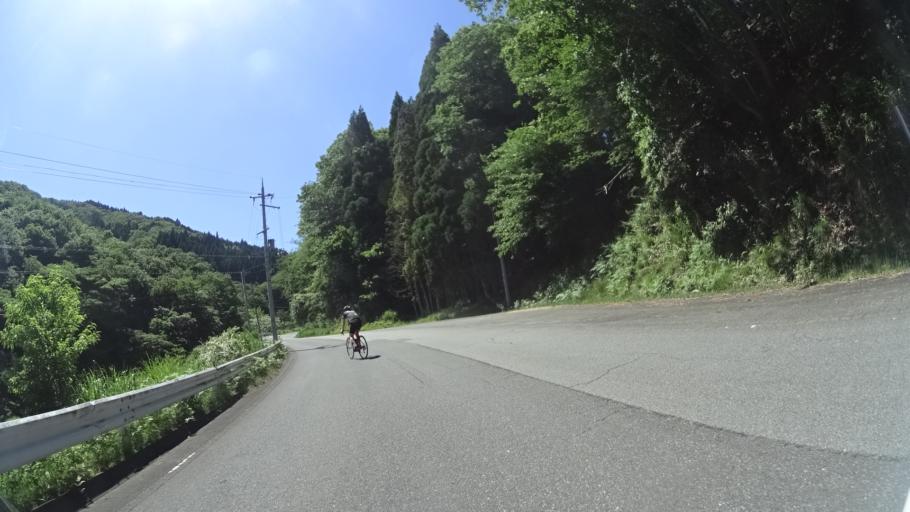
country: JP
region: Kyoto
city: Fukuchiyama
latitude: 35.4273
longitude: 135.0542
